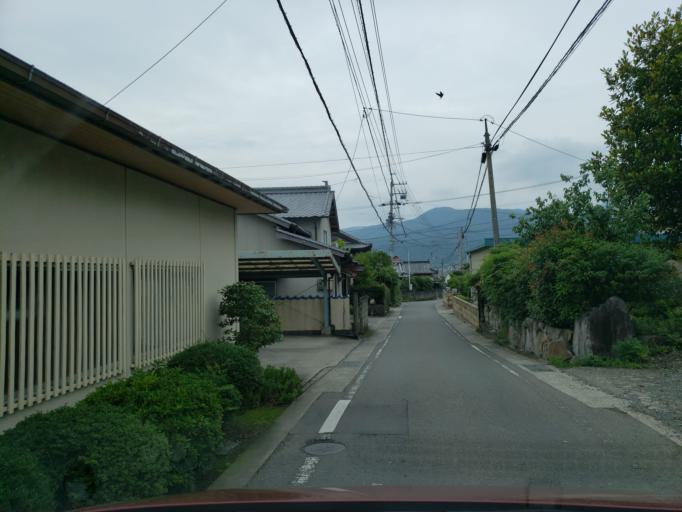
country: JP
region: Tokushima
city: Kamojimacho-jogejima
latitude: 34.0996
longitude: 134.2813
